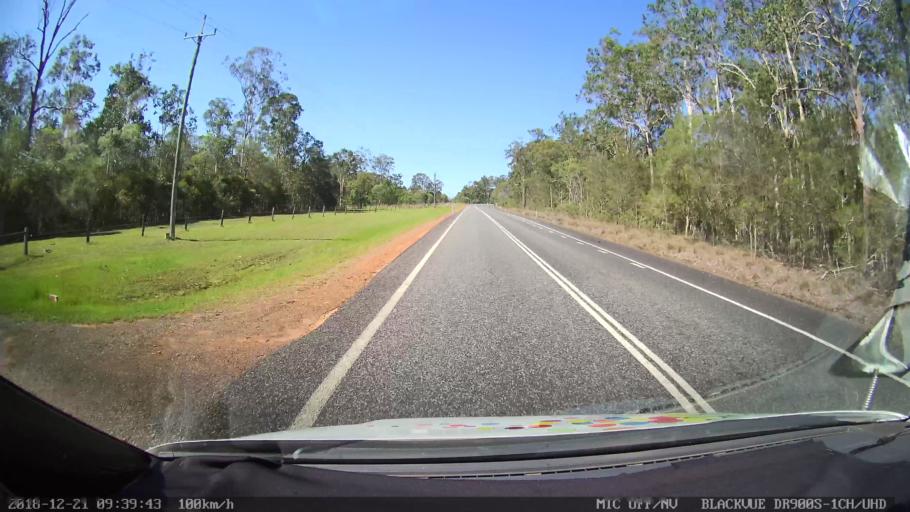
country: AU
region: New South Wales
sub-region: Clarence Valley
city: Grafton
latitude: -29.5641
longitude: 152.9697
